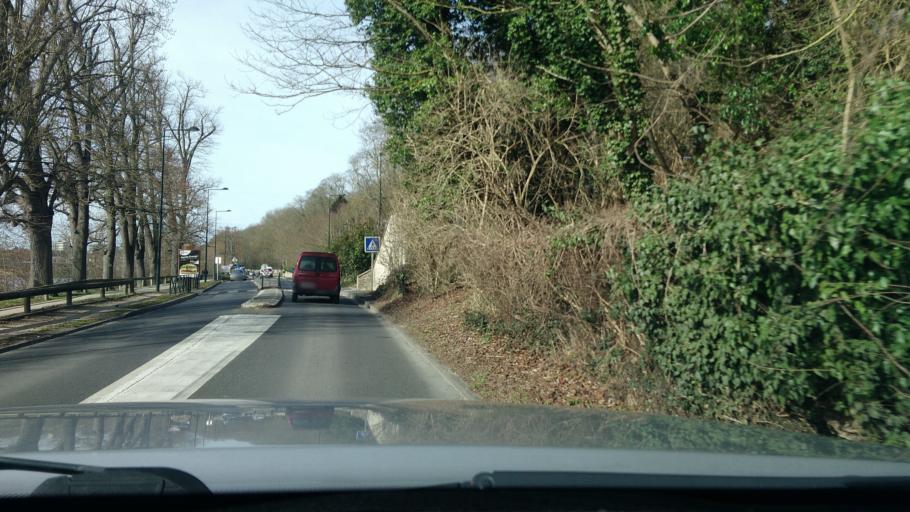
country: FR
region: Ile-de-France
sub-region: Departement de Seine-et-Marne
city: Melun
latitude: 48.5307
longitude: 2.6694
